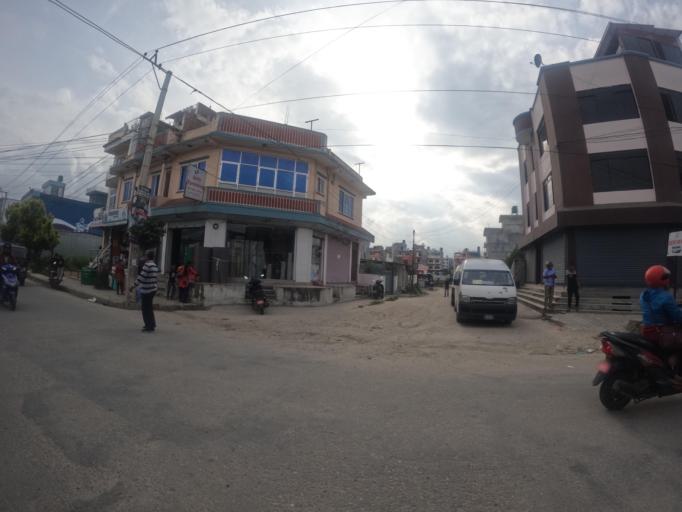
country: NP
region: Central Region
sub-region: Bagmati Zone
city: Bhaktapur
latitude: 27.6792
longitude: 85.3986
